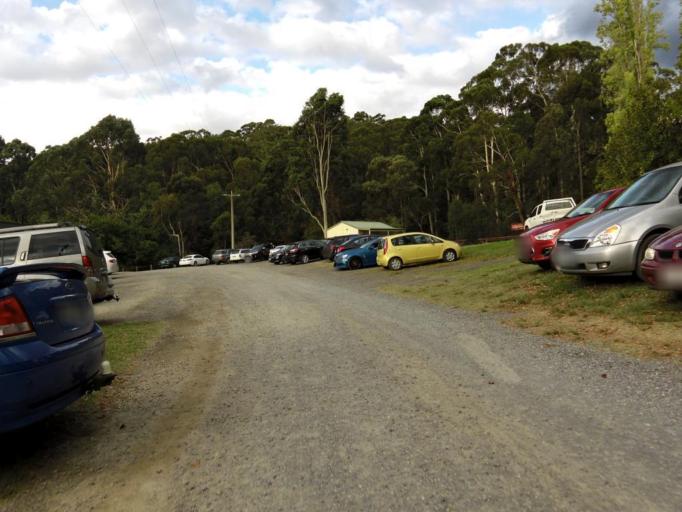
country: AU
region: Victoria
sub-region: Yarra Ranges
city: Mount Evelyn
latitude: -37.7961
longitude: 145.3825
